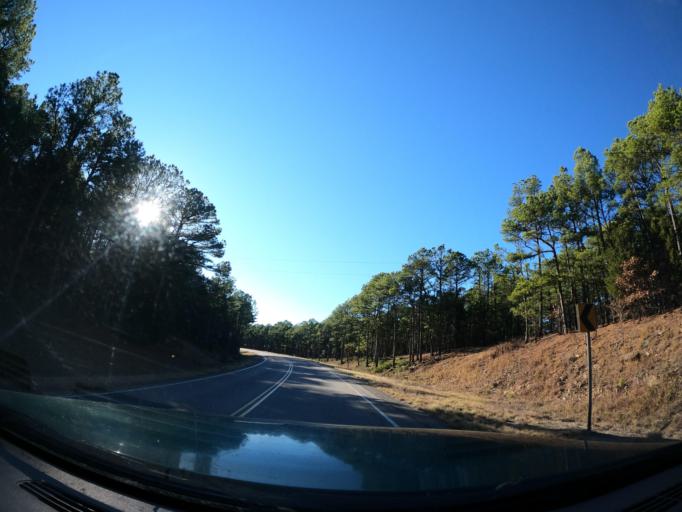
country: US
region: Oklahoma
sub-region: Latimer County
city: Wilburton
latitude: 35.0010
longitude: -95.3401
